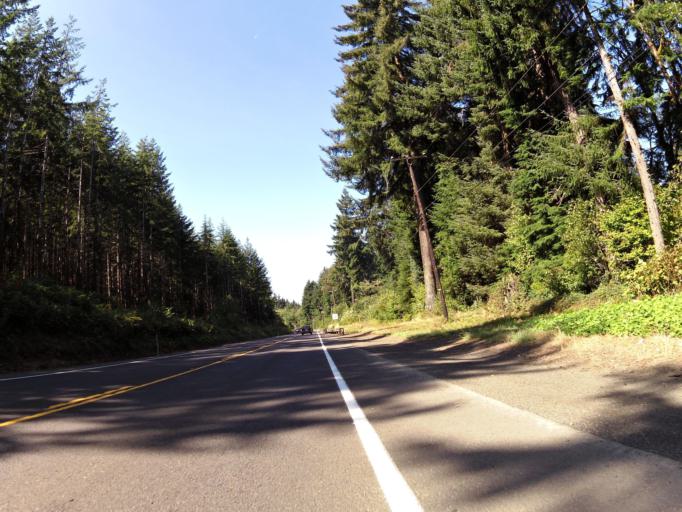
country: US
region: Washington
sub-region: Wahkiakum County
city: Cathlamet
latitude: 46.1763
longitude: -123.5112
